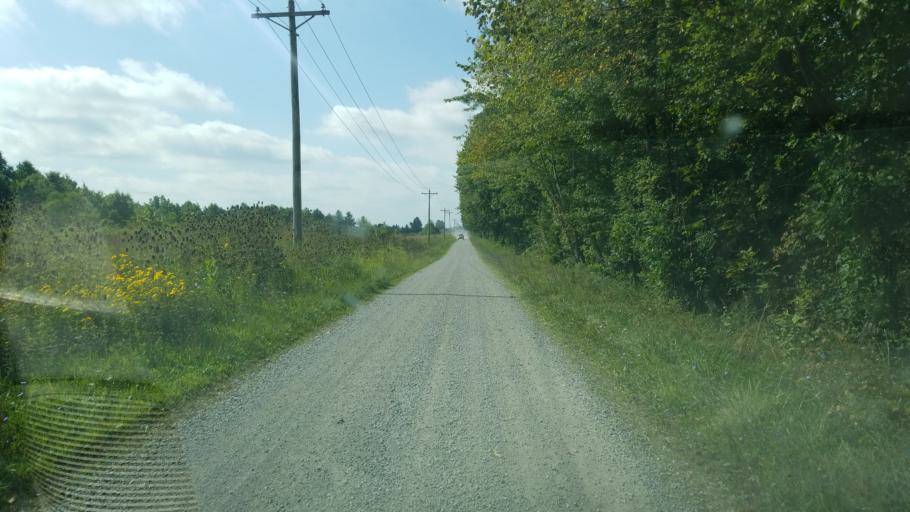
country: US
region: Ohio
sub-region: Wyandot County
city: Upper Sandusky
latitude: 40.7050
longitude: -83.3622
